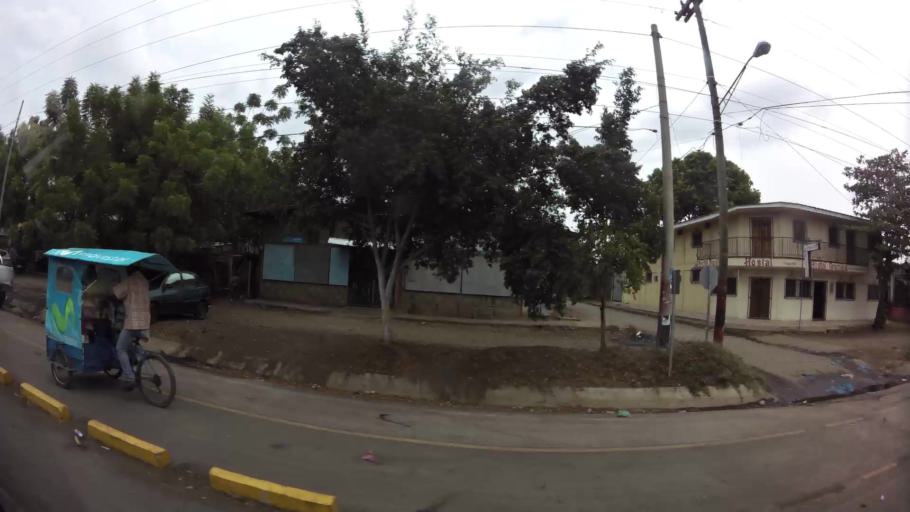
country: NI
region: Leon
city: Leon
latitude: 12.4491
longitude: -86.8635
